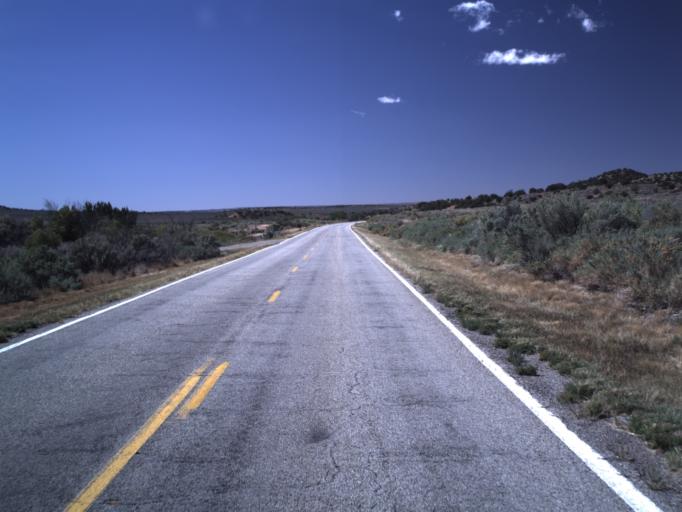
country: US
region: Utah
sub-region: Grand County
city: Moab
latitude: 38.3057
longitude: -109.3647
